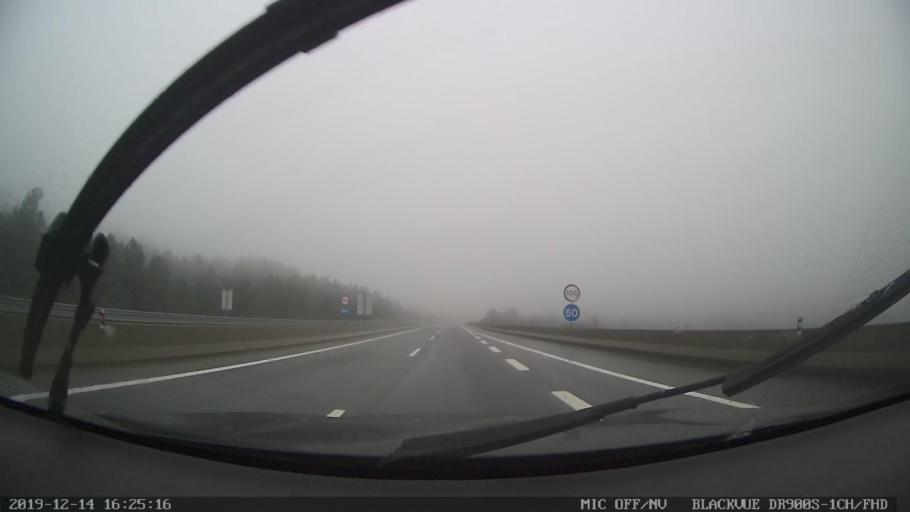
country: PT
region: Vila Real
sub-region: Vila Real
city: Vila Real
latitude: 41.3200
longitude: -7.6570
